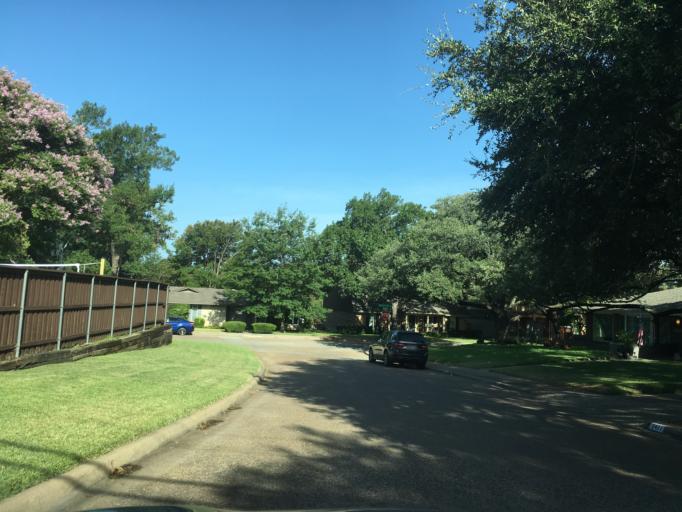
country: US
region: Texas
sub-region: Dallas County
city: Richardson
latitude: 32.8804
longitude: -96.7283
